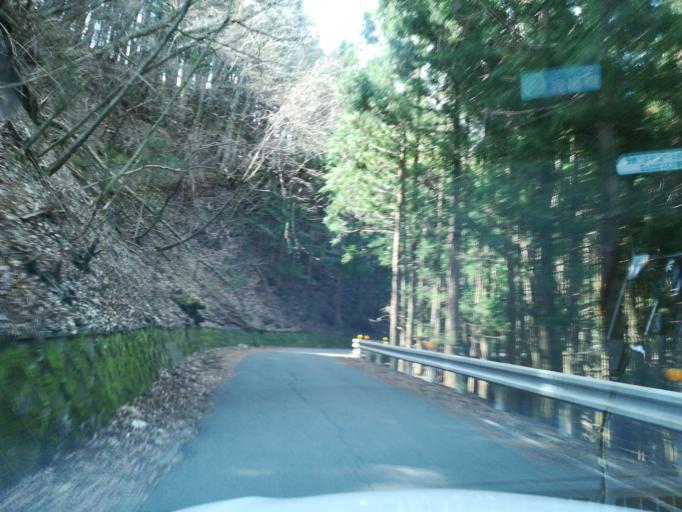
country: JP
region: Tokushima
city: Wakimachi
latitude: 33.8872
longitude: 134.0537
